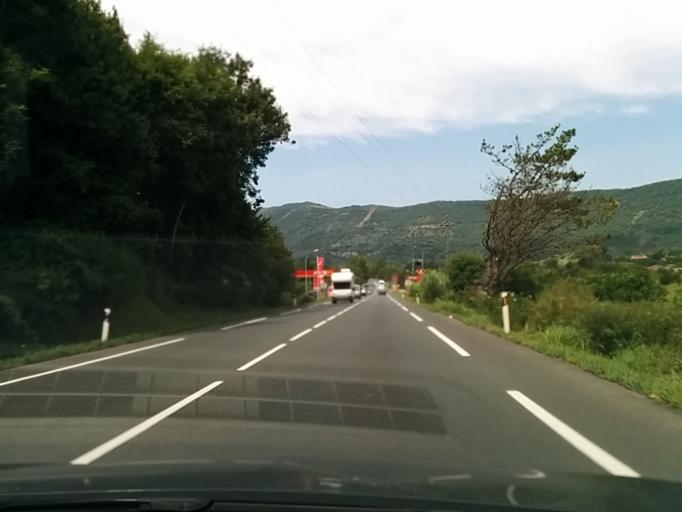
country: ES
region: Basque Country
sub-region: Provincia de Guipuzcoa
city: Irun
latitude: 43.3472
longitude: -1.8059
